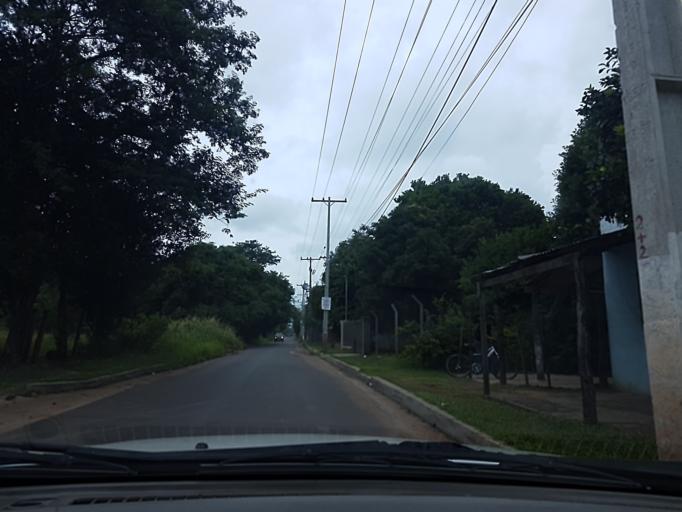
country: PY
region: Central
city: Limpio
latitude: -25.1832
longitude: -57.4724
